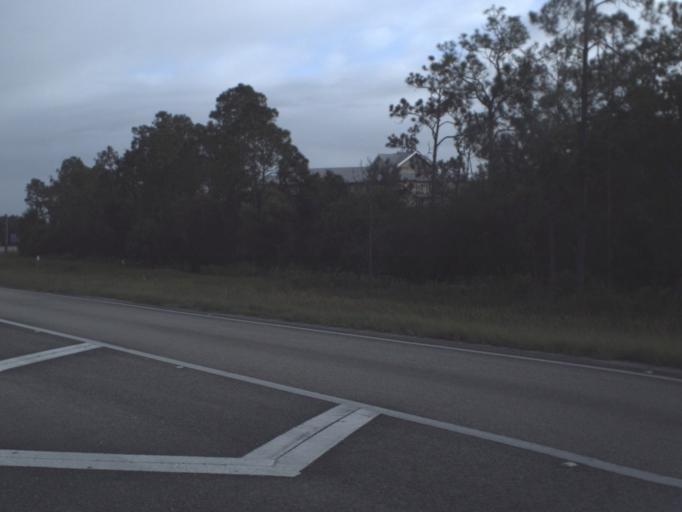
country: US
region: Florida
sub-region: Lee County
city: Fort Myers
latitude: 26.6076
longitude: -81.8015
